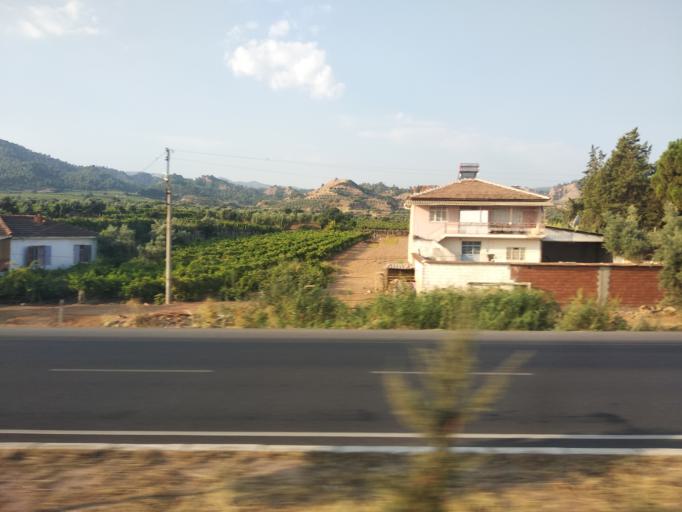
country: TR
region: Manisa
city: Ahmetli
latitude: 38.5046
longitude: 28.0062
